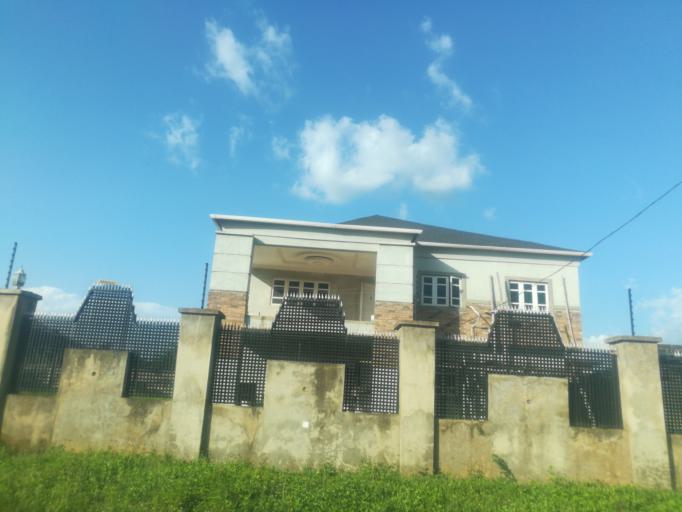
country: NG
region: Oyo
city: Ibadan
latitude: 7.4366
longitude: 3.9702
